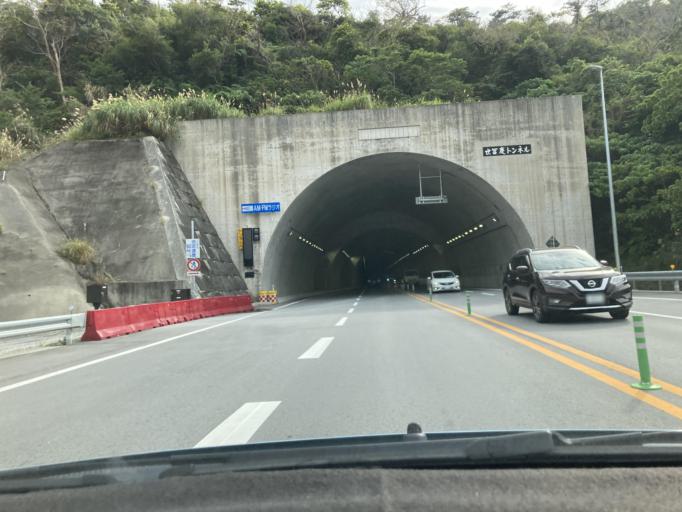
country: JP
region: Okinawa
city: Nago
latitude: 26.5722
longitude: 127.9891
